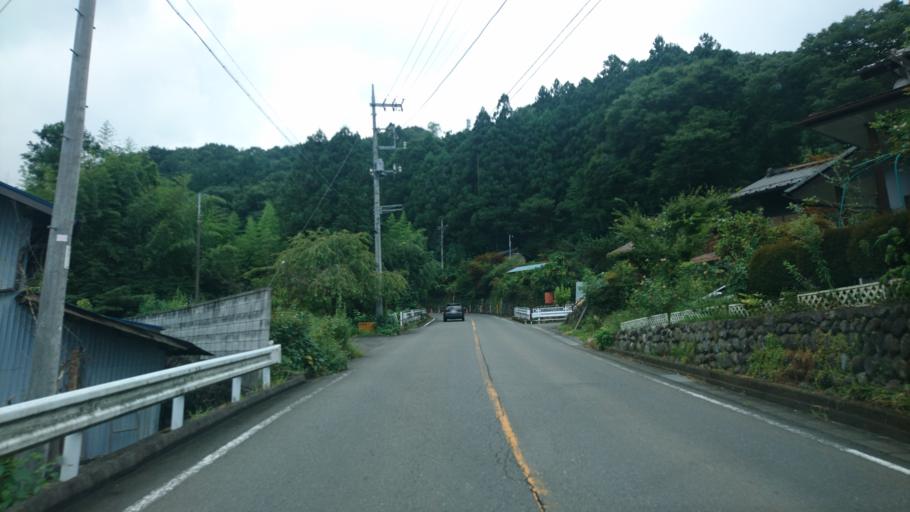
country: JP
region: Gunma
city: Omamacho-omama
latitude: 36.4953
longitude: 139.2750
